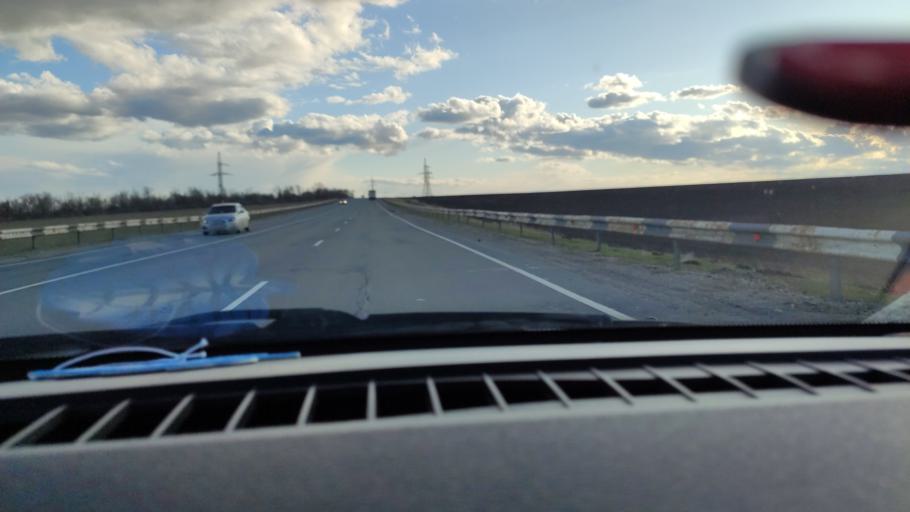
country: RU
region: Saratov
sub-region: Saratovskiy Rayon
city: Saratov
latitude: 51.7477
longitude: 46.0558
